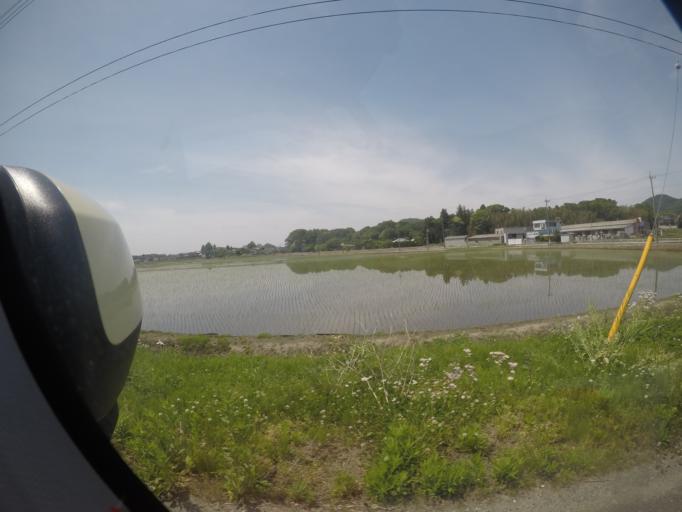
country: JP
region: Ibaraki
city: Iwase
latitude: 36.3238
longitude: 140.1123
